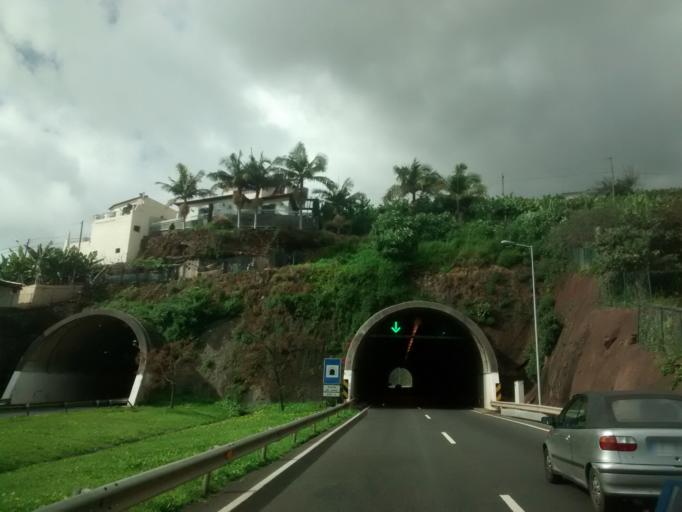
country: PT
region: Madeira
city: Camara de Lobos
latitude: 32.6609
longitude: -16.9774
